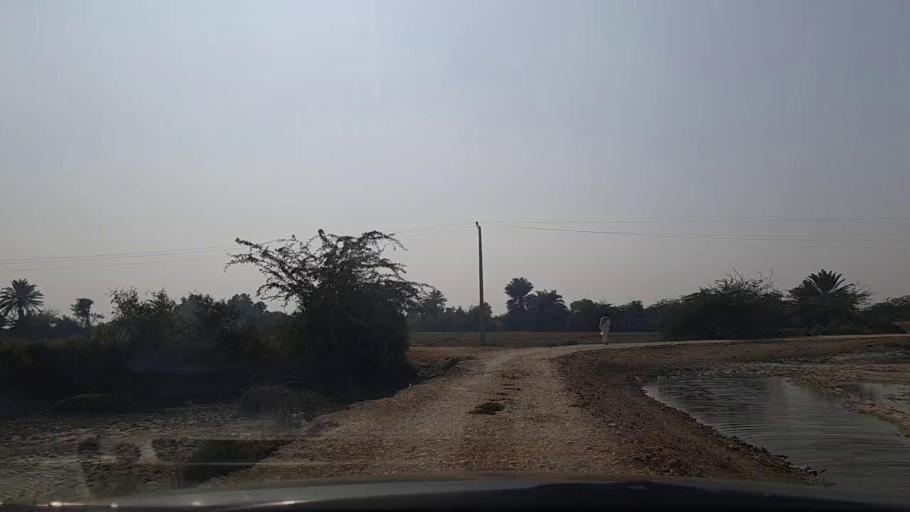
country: PK
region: Sindh
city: Mirpur Sakro
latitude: 24.5628
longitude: 67.7760
